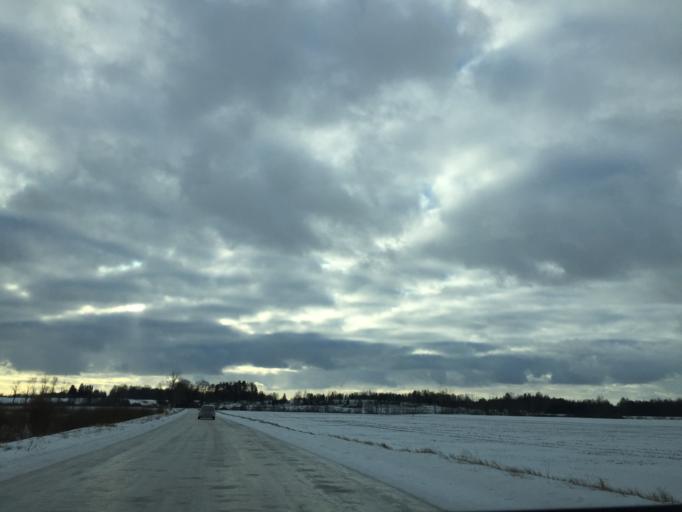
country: LV
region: Lielvarde
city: Lielvarde
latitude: 56.5871
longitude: 24.7343
